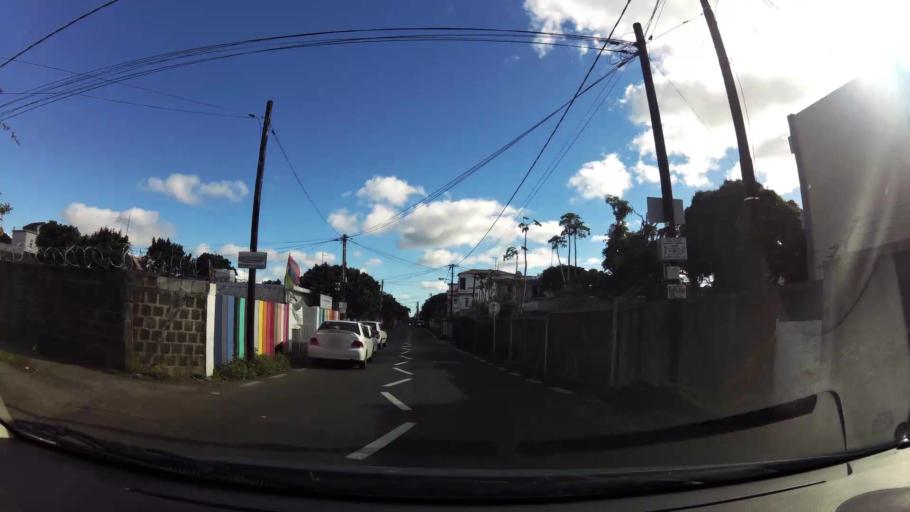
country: MU
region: Plaines Wilhems
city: Vacoas
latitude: -20.2961
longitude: 57.4893
